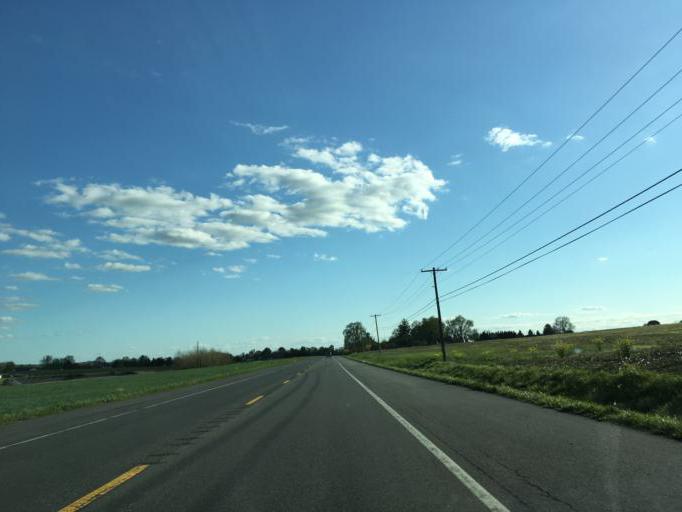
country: US
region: Maryland
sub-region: Frederick County
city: Walkersville
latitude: 39.4971
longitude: -77.3288
